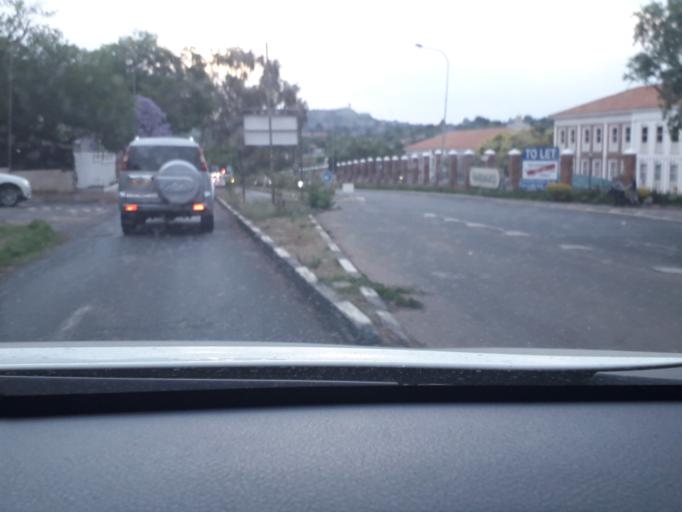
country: ZA
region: Gauteng
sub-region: City of Johannesburg Metropolitan Municipality
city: Johannesburg
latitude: -26.1428
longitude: 28.0099
